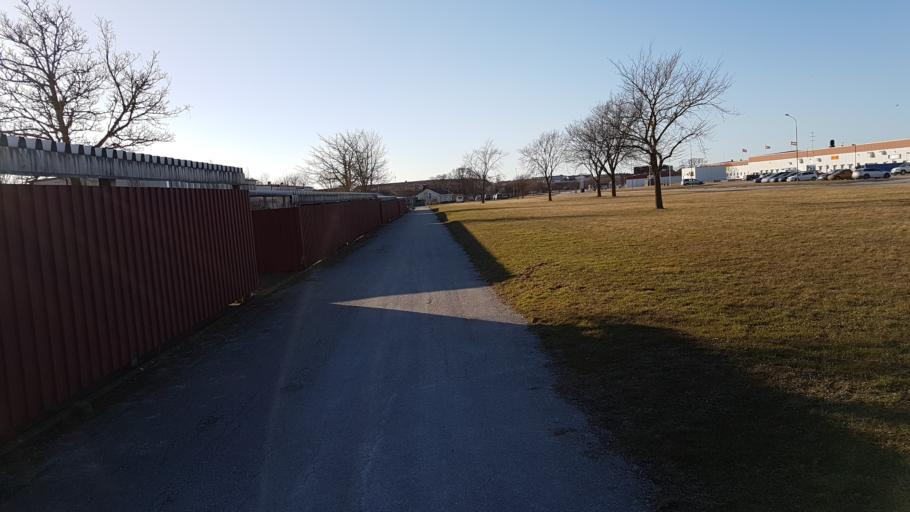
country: SE
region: Gotland
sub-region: Gotland
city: Visby
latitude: 57.6409
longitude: 18.3226
